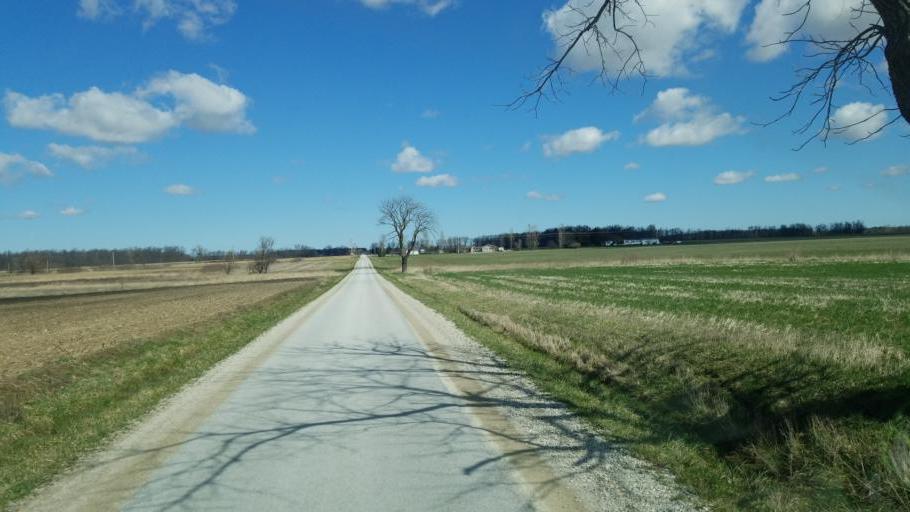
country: US
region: Ohio
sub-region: Sandusky County
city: Mount Carmel
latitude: 41.2084
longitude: -82.9373
